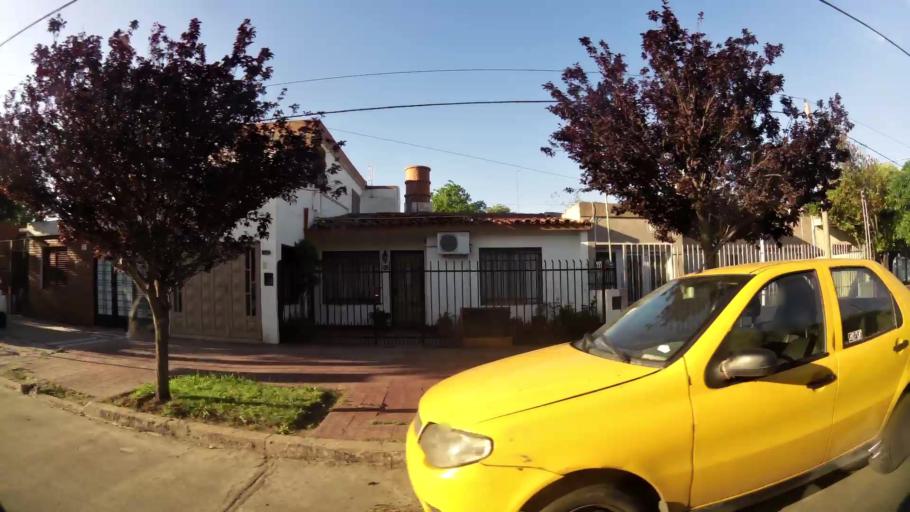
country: AR
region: Cordoba
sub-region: Departamento de Capital
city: Cordoba
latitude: -31.3782
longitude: -64.1945
